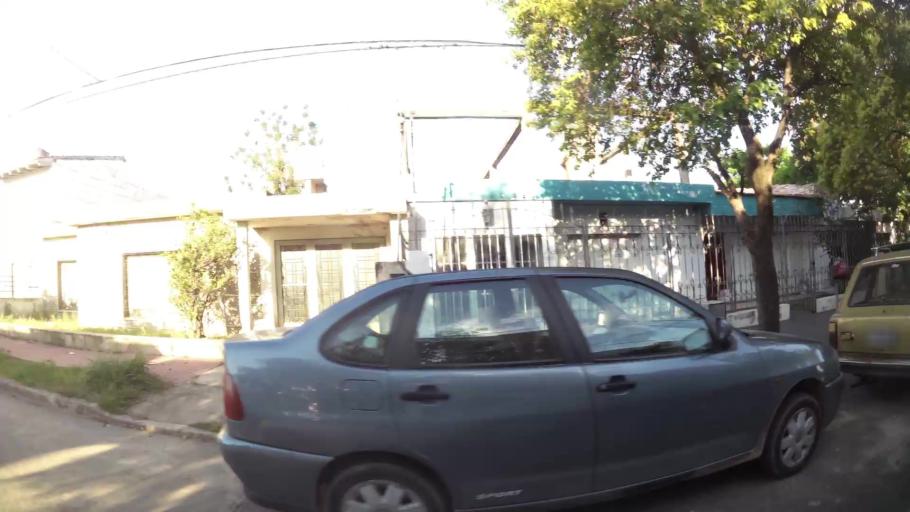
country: AR
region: Cordoba
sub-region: Departamento de Capital
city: Cordoba
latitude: -31.3930
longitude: -64.2163
